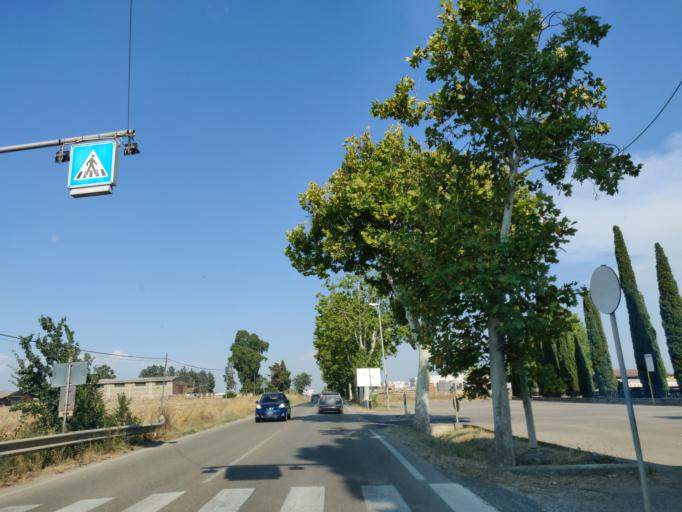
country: IT
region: Latium
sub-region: Provincia di Viterbo
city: Montalto di Castro
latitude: 42.3502
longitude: 11.6205
